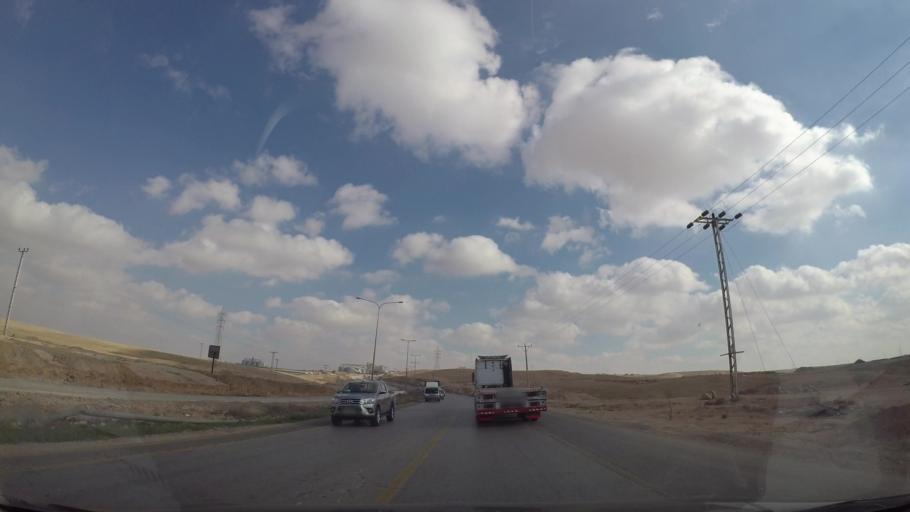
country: JO
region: Amman
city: Al Jizah
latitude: 31.6299
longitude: 35.9864
